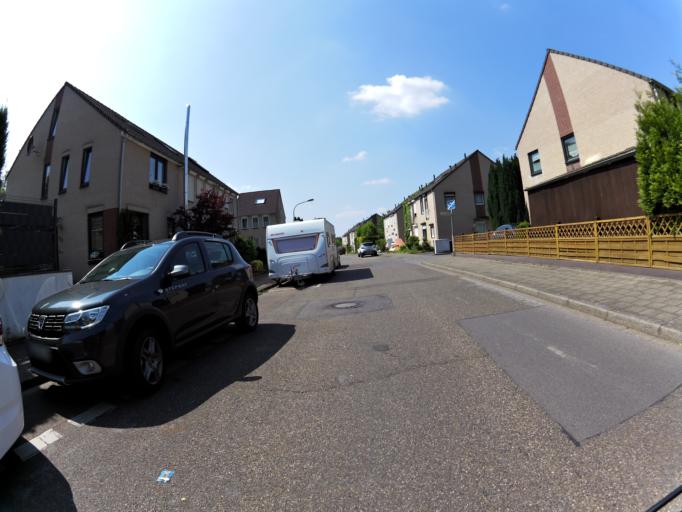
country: DE
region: North Rhine-Westphalia
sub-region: Regierungsbezirk Koln
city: Herzogenrath
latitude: 50.8977
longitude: 6.1195
